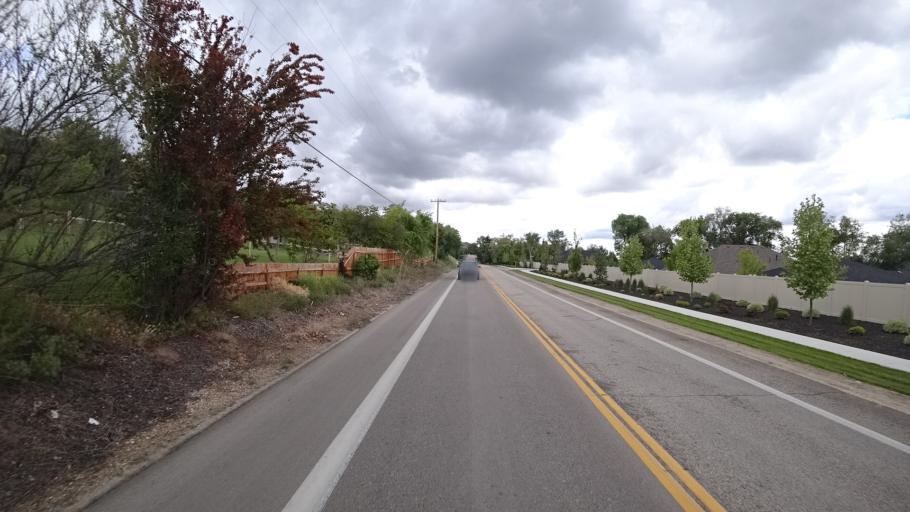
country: US
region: Idaho
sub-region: Ada County
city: Garden City
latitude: 43.6770
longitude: -116.2655
